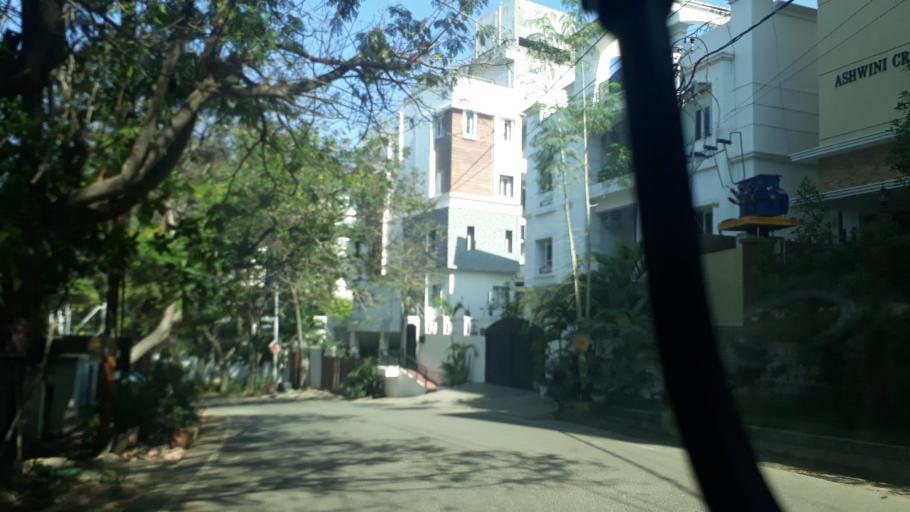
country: IN
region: Telangana
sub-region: Rangareddi
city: Kukatpalli
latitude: 17.4217
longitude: 78.4024
